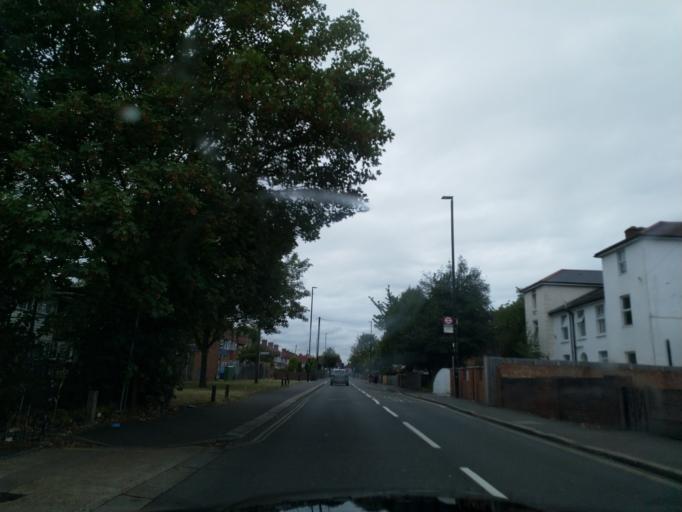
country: GB
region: England
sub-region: Greater London
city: Hounslow
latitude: 51.4624
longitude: -0.3763
